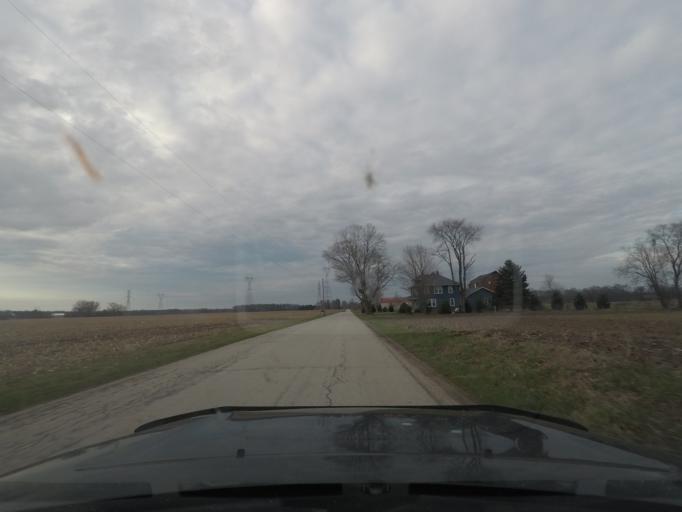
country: US
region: Indiana
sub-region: LaPorte County
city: LaPorte
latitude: 41.5531
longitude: -86.7986
